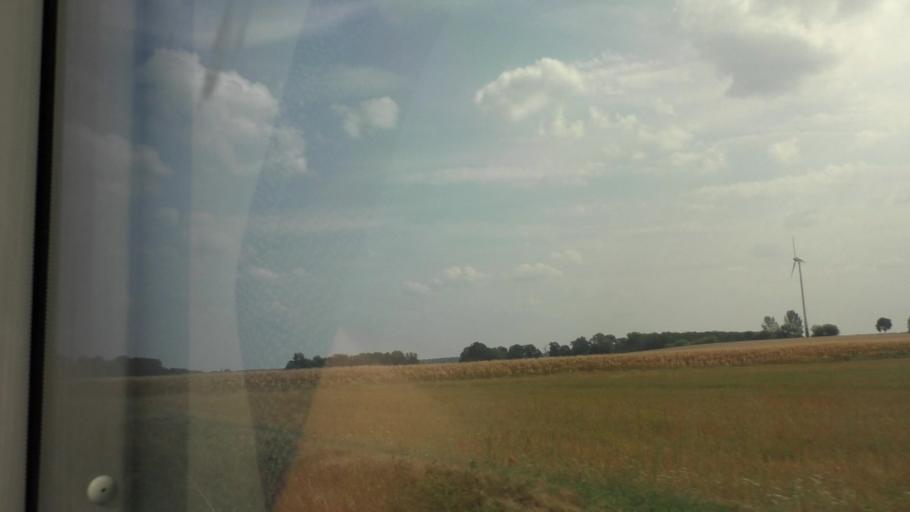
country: DE
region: Brandenburg
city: Beeskow
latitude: 52.1712
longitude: 14.2921
